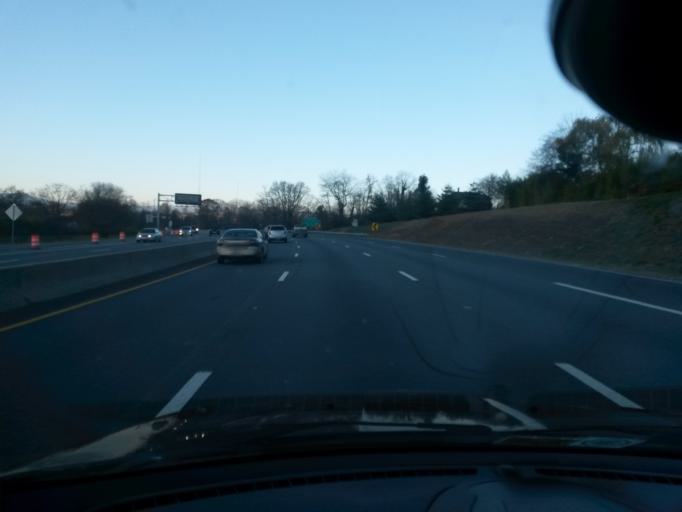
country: US
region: Virginia
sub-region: City of Roanoke
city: Roanoke
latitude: 37.2582
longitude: -79.9491
